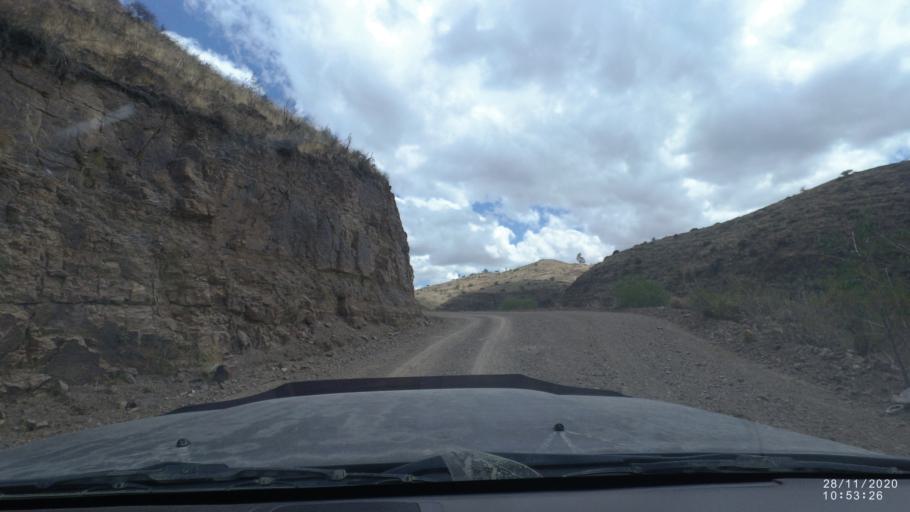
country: BO
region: Cochabamba
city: Capinota
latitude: -17.7811
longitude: -66.1190
